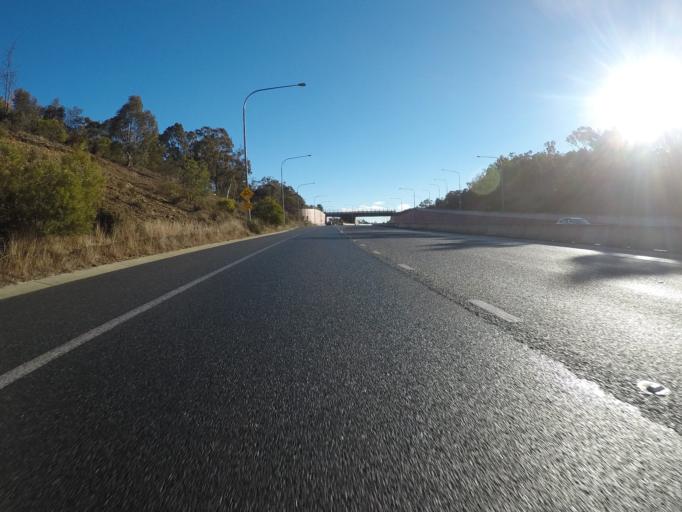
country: AU
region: Australian Capital Territory
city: Macquarie
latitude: -35.2638
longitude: 149.0859
